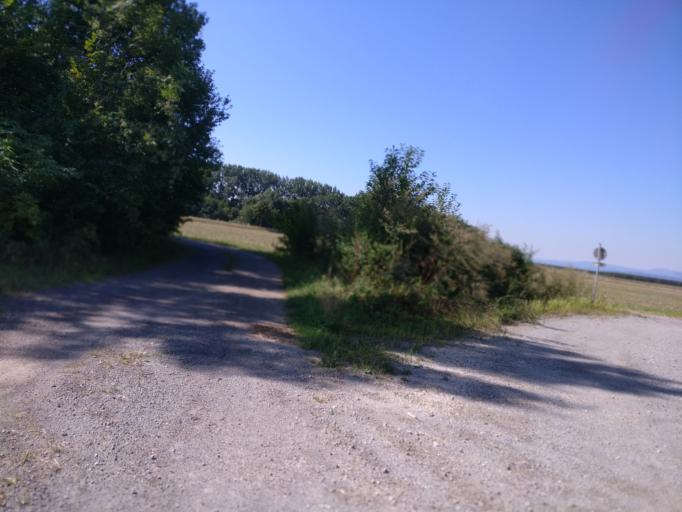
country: AT
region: Lower Austria
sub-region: Politischer Bezirk Baden
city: Pottendorf
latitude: 47.9253
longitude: 16.3668
